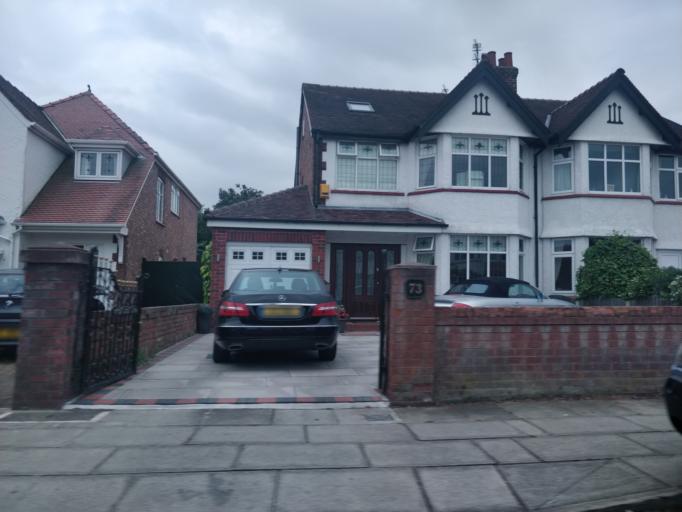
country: GB
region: England
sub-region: Sefton
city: Southport
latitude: 53.6585
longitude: -2.9687
